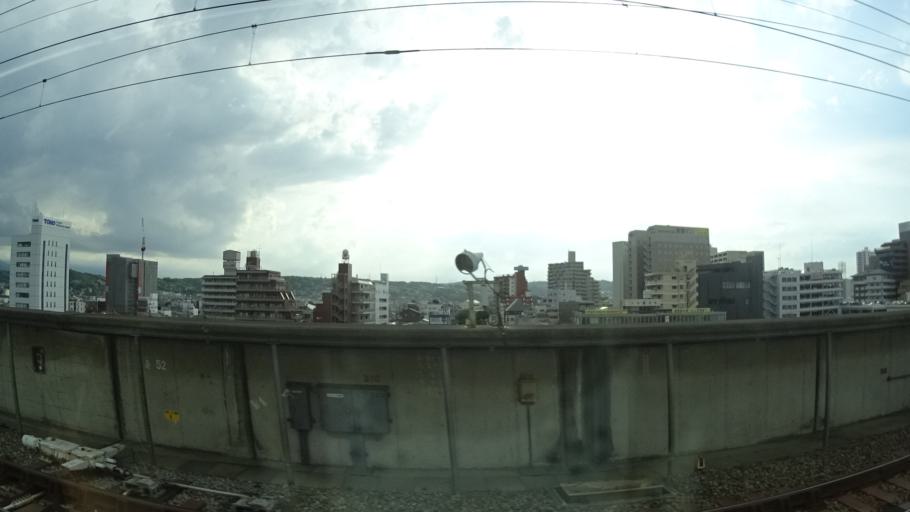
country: JP
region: Gunma
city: Takasaki
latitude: 36.3200
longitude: 139.0133
